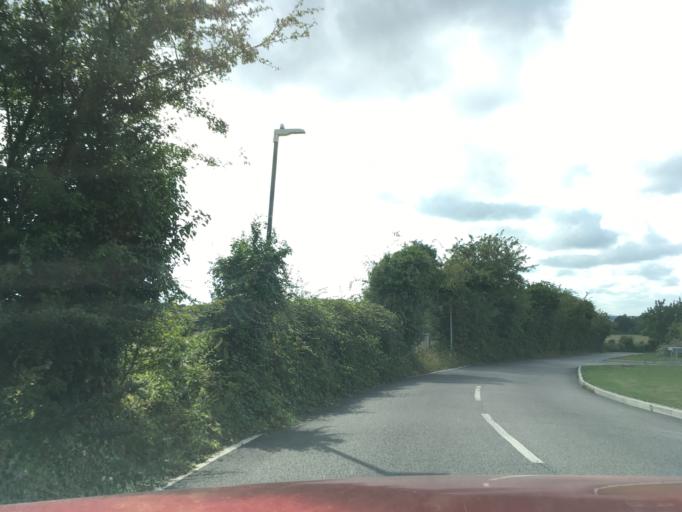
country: GB
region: England
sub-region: Kent
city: Maidstone
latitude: 51.2530
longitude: 0.5222
